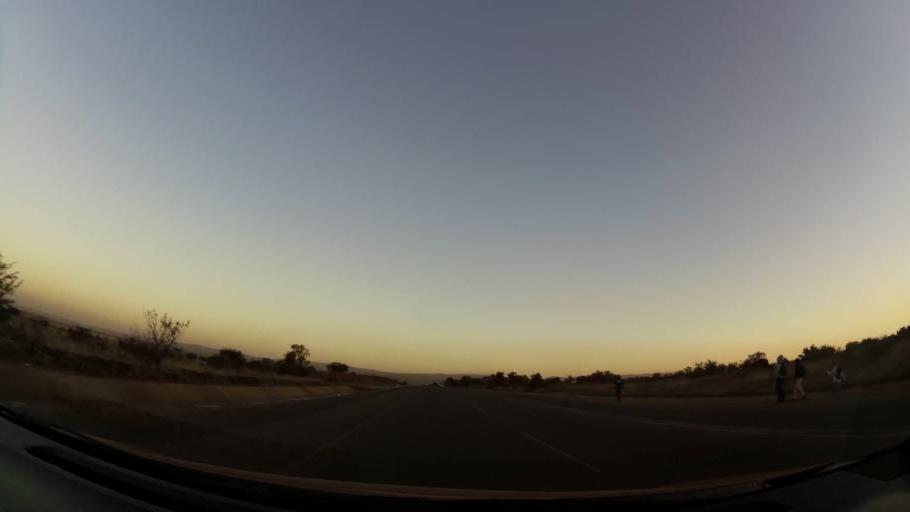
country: ZA
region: North-West
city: Ga-Rankuwa
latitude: -25.6091
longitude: 28.0389
